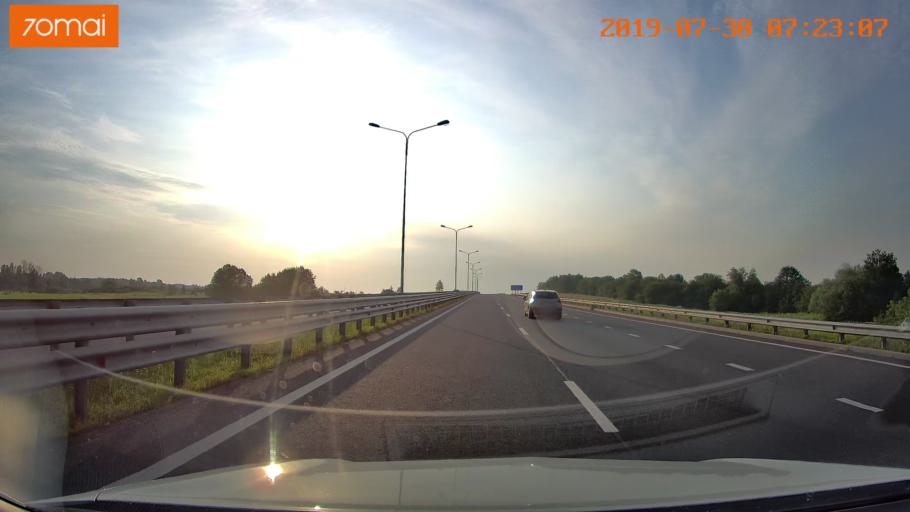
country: RU
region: Kaliningrad
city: Bol'shoe Isakovo
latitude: 54.6919
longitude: 20.7750
